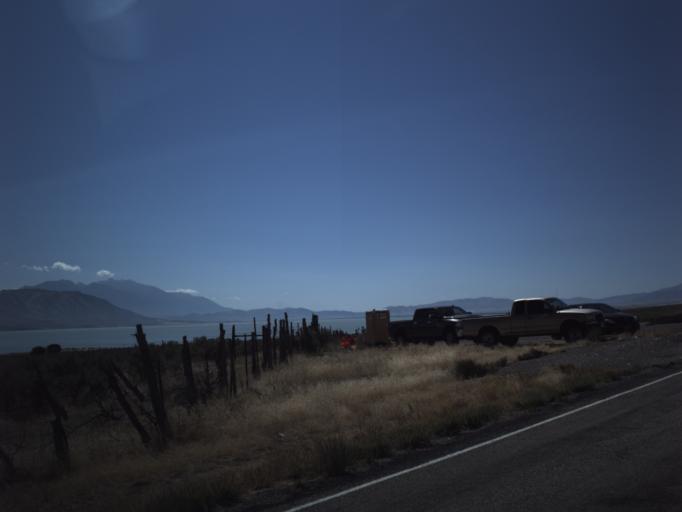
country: US
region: Utah
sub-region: Utah County
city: Saratoga Springs
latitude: 40.1990
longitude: -111.9016
